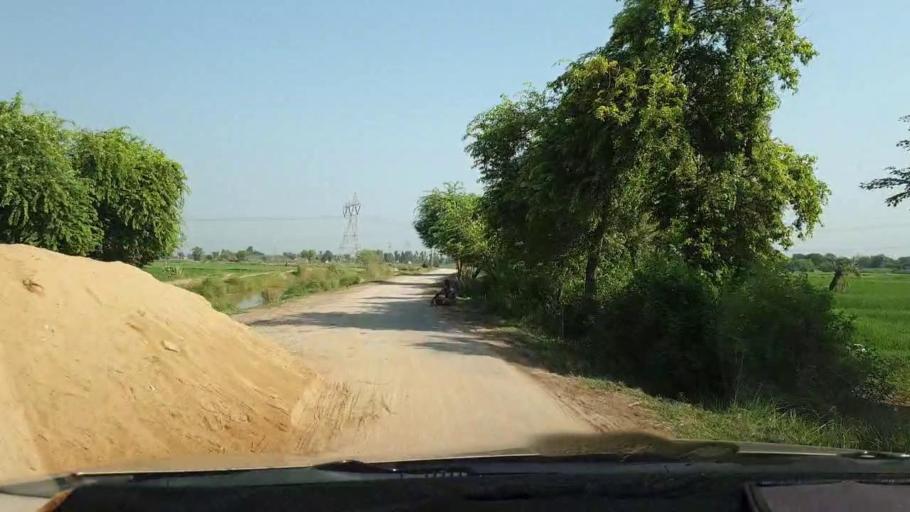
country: PK
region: Sindh
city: Larkana
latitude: 27.6363
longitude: 68.2367
